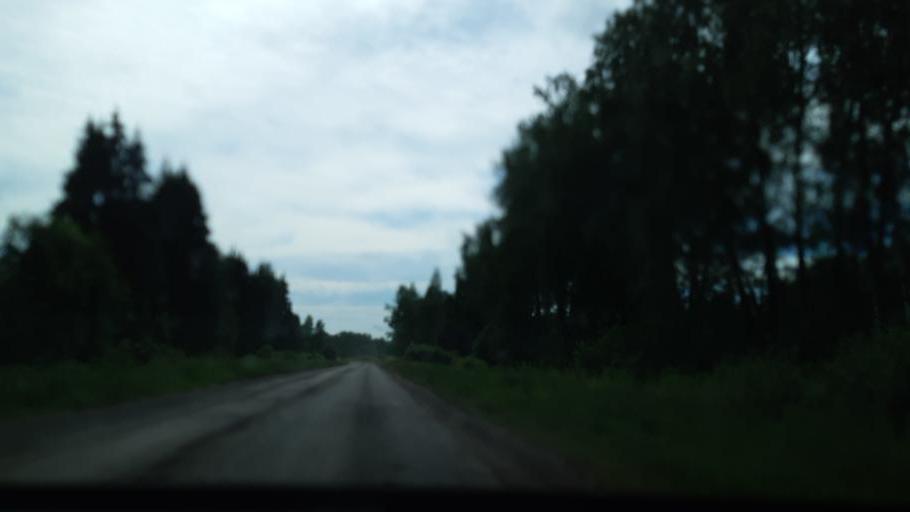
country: RU
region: Moskovskaya
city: Vereya
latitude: 55.3177
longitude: 36.1288
